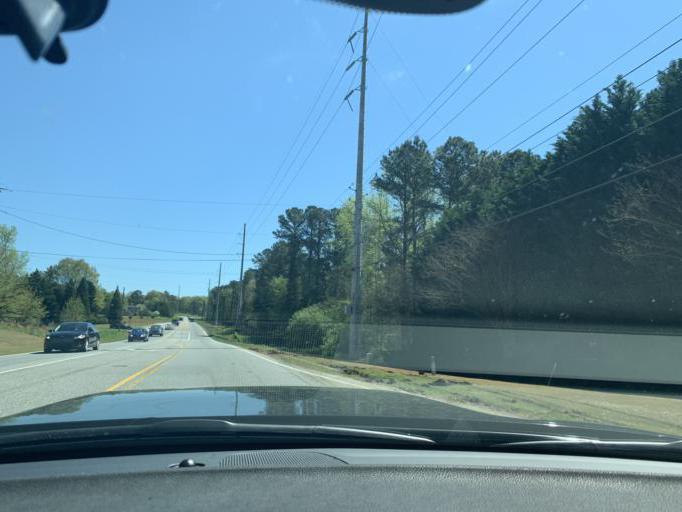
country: US
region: Georgia
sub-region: Forsyth County
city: Cumming
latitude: 34.1599
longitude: -84.1886
